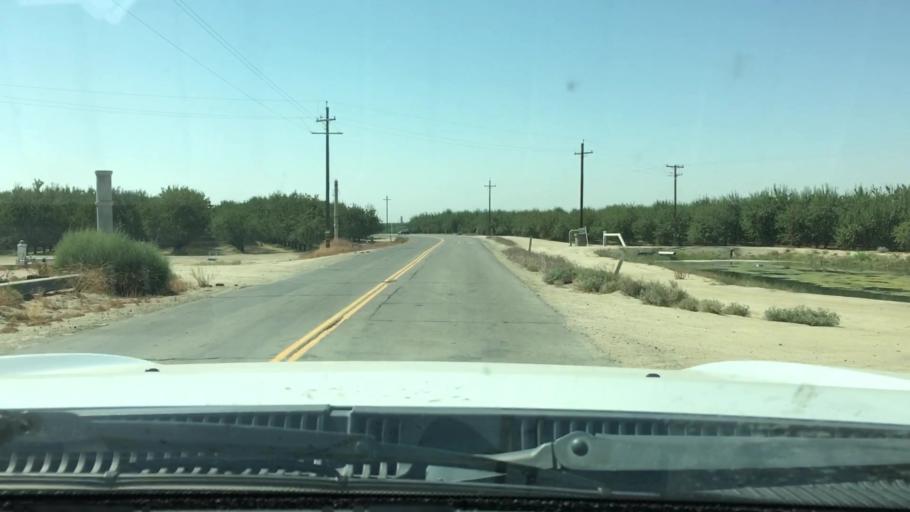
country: US
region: California
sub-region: Kern County
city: Shafter
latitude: 35.5496
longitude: -119.2771
